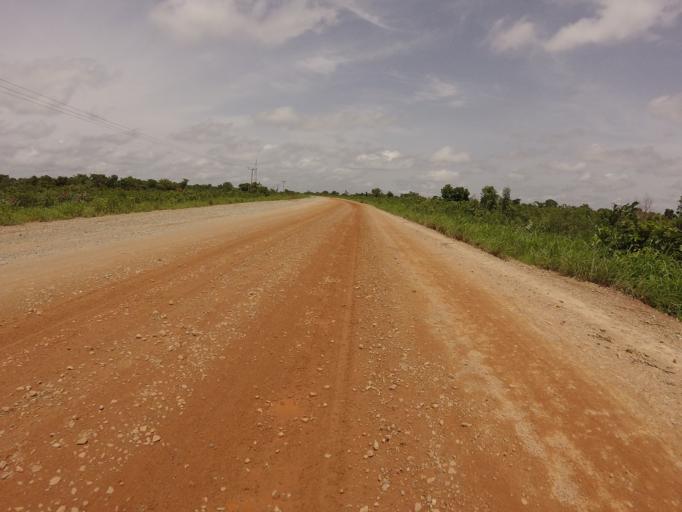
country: GH
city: Kpandae
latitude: 8.5830
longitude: 0.2391
